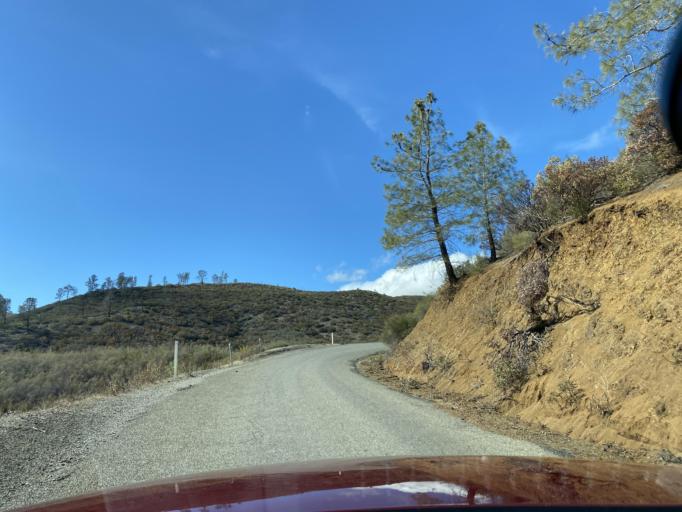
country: US
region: California
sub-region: Lake County
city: Lucerne
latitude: 39.3648
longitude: -122.6292
